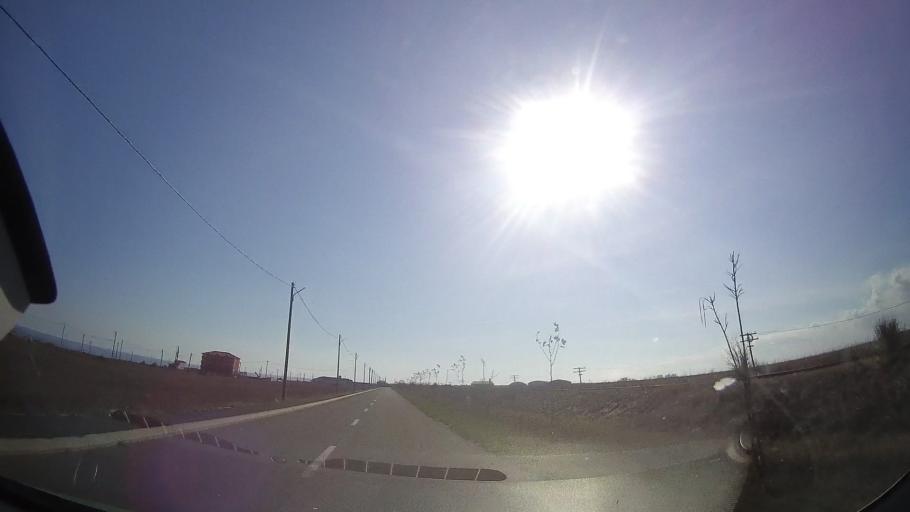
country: RO
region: Constanta
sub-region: Comuna Costinesti
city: Schitu
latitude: 43.9298
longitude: 28.6318
